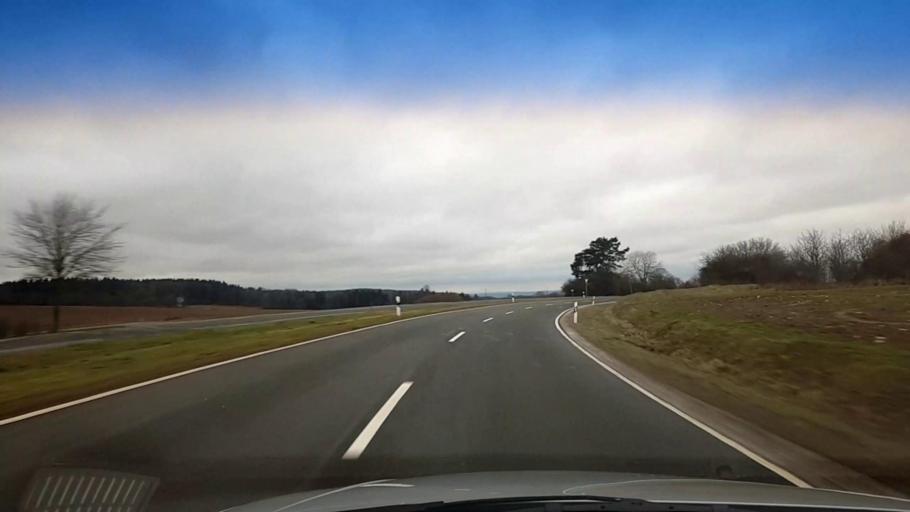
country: DE
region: Bavaria
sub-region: Upper Franconia
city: Wattendorf
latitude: 50.0390
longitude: 11.0989
